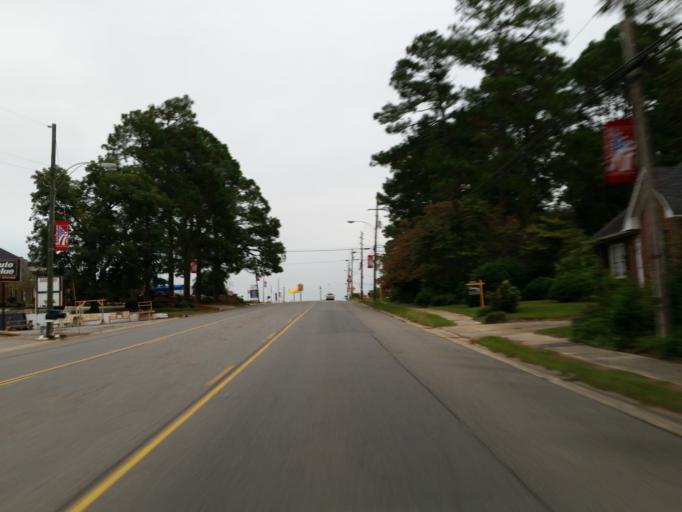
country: US
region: Georgia
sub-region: Turner County
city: Ashburn
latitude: 31.7090
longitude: -83.6450
